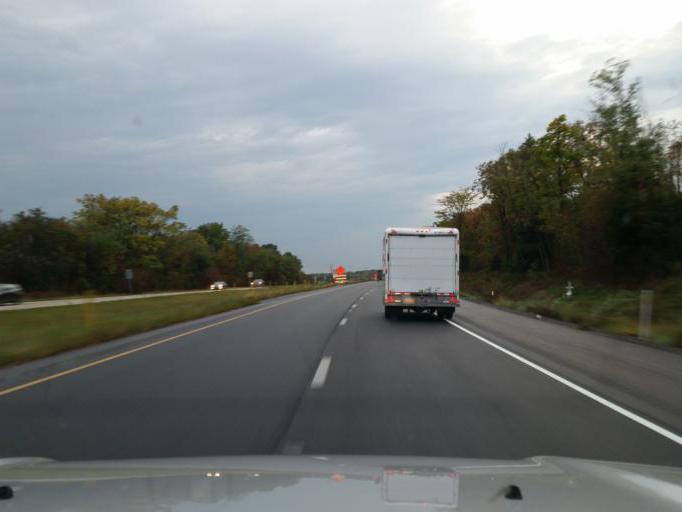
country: US
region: Pennsylvania
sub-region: Adams County
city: Lake Heritage
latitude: 39.8066
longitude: -77.1958
